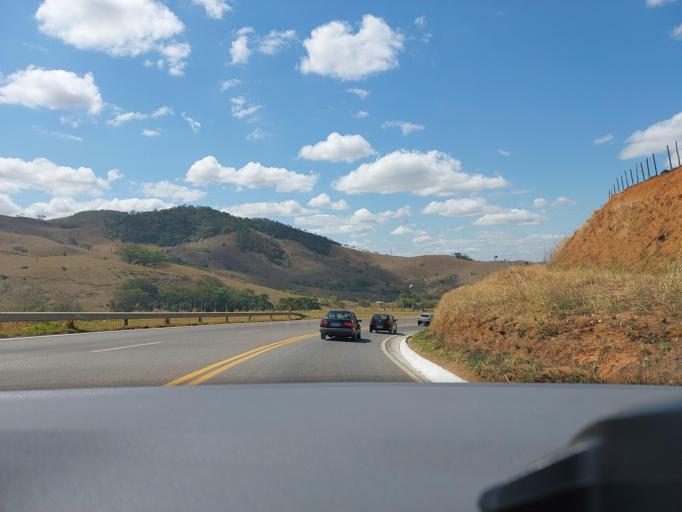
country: BR
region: Minas Gerais
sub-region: Muriae
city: Muriae
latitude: -21.0906
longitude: -42.4776
